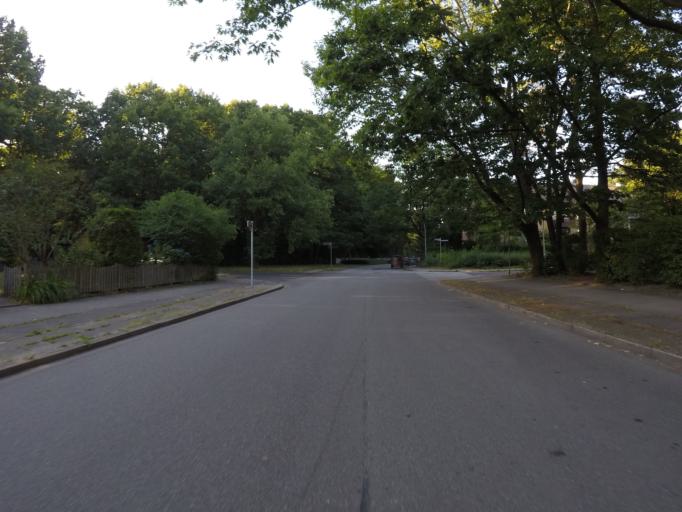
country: DE
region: Hamburg
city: Poppenbuettel
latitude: 53.6619
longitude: 10.0965
